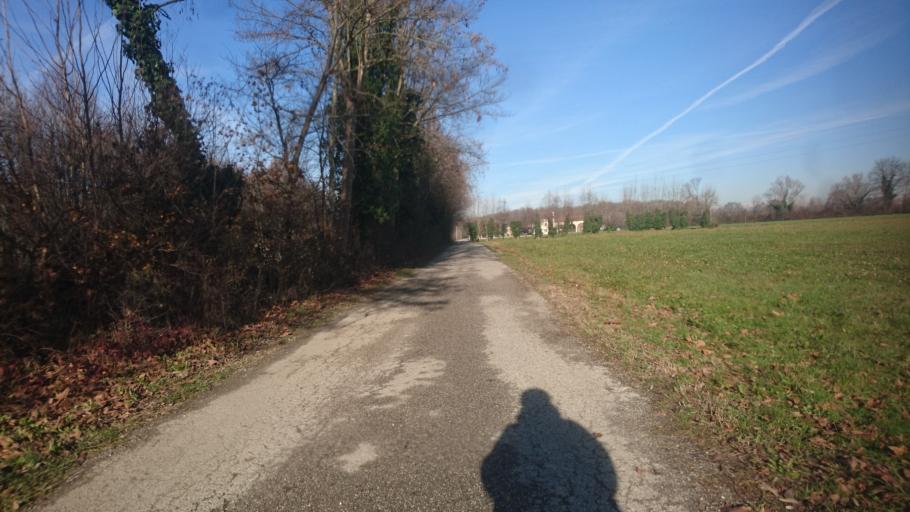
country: IT
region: Veneto
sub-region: Provincia di Padova
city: Piazzola sul Brenta
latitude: 45.5165
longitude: 11.7785
